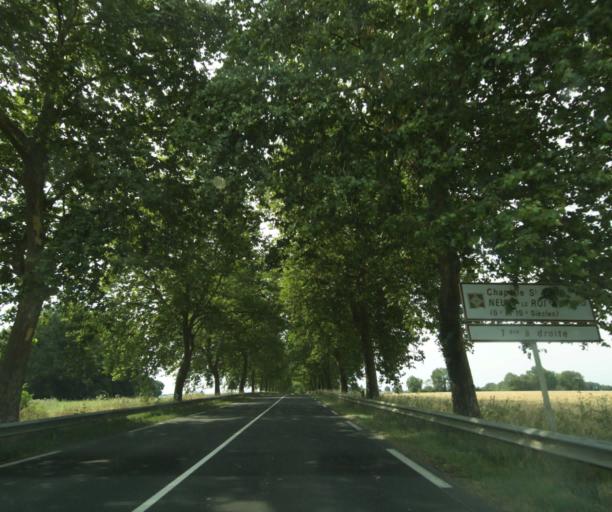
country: FR
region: Centre
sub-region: Departement d'Indre-et-Loire
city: Neuille-Pont-Pierre
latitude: 47.5901
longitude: 0.5361
